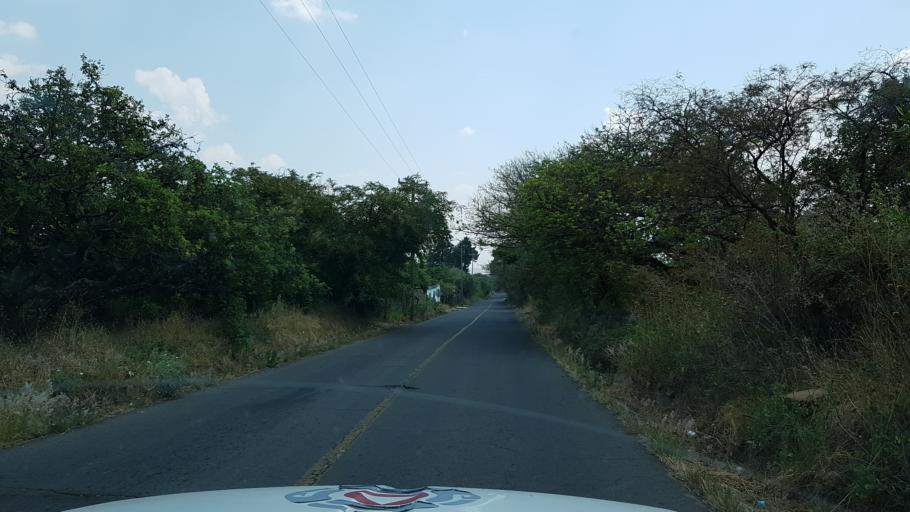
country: MX
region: Morelos
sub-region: Yecapixtla
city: Texcala
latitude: 18.9178
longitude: -98.8078
